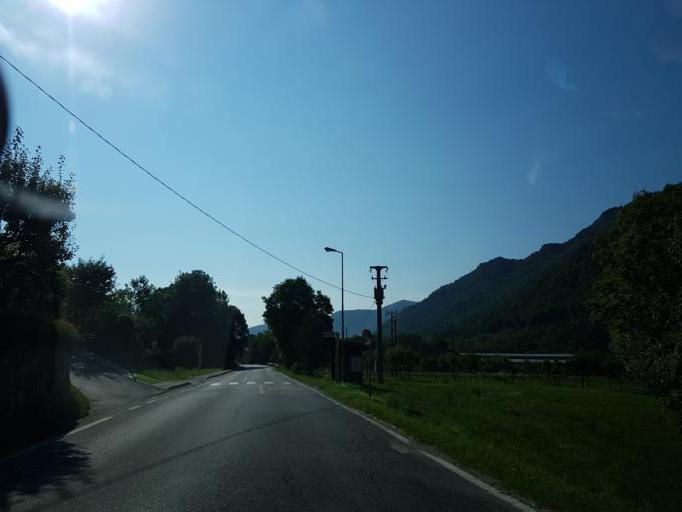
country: IT
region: Piedmont
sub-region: Provincia di Cuneo
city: San Damiano Macra
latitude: 44.4865
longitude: 7.2703
